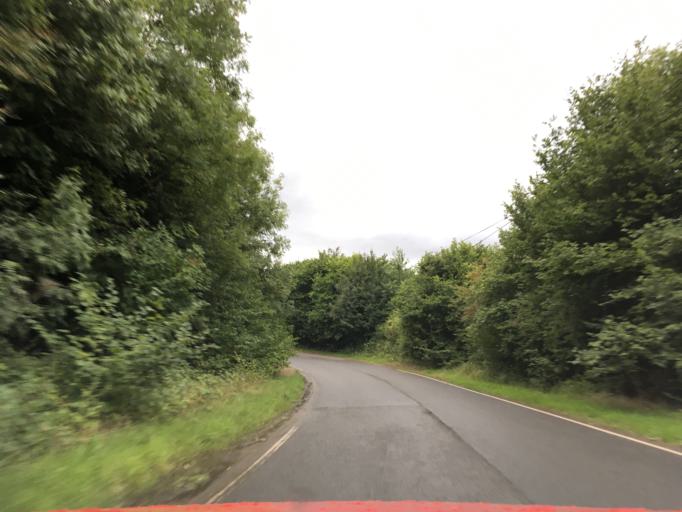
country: GB
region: Wales
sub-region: Monmouthshire
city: Llangybi
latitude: 51.6347
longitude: -2.8896
